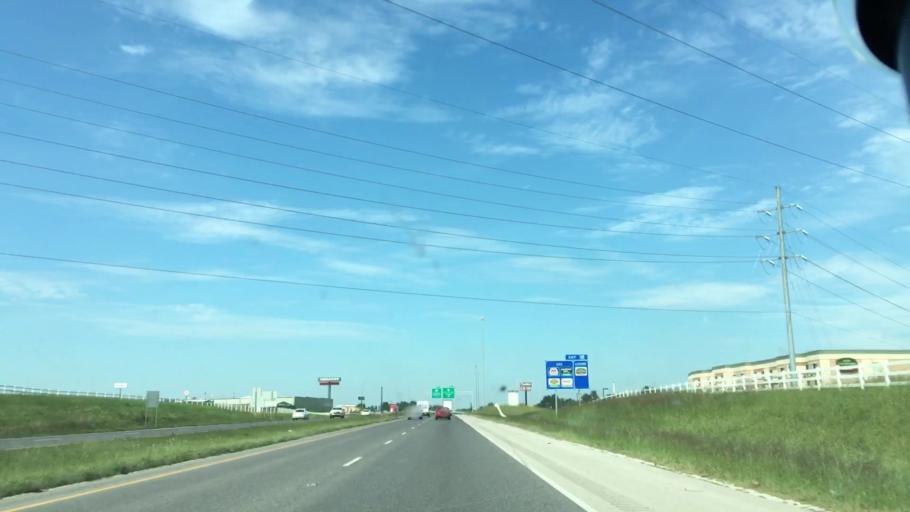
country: US
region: Kentucky
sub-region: Daviess County
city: Owensboro
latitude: 37.7503
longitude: -87.0712
